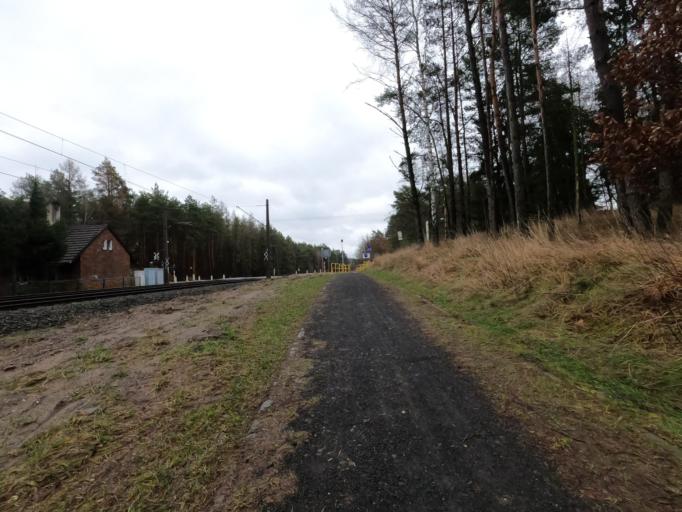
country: PL
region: Greater Poland Voivodeship
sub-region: Powiat pilski
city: Kaczory
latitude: 53.1099
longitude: 16.8647
